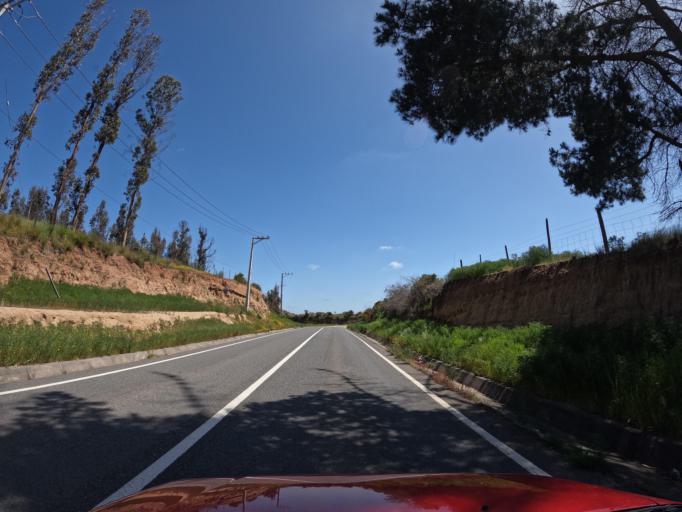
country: CL
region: O'Higgins
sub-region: Provincia de Colchagua
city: Santa Cruz
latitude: -34.6615
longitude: -71.8426
